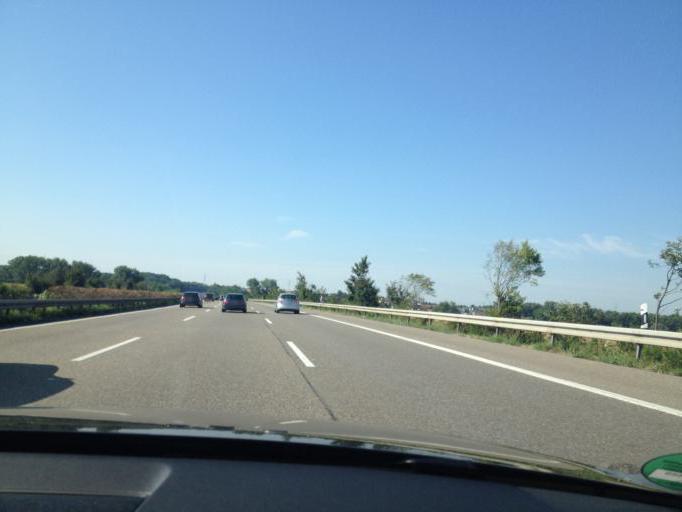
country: DE
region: Baden-Wuerttemberg
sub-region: Regierungsbezirk Stuttgart
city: Pleidelsheim
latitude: 48.9471
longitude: 9.1995
